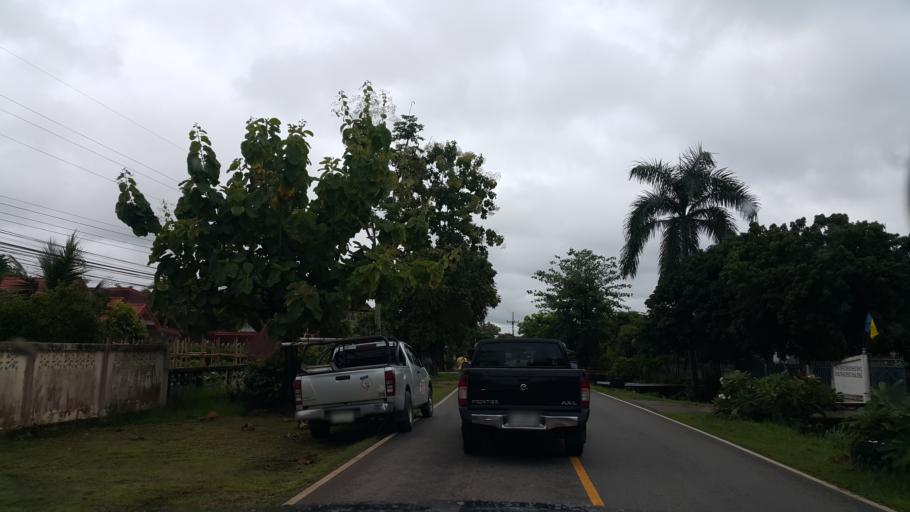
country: TH
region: Phayao
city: Chiang Kham
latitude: 19.5231
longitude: 100.3514
